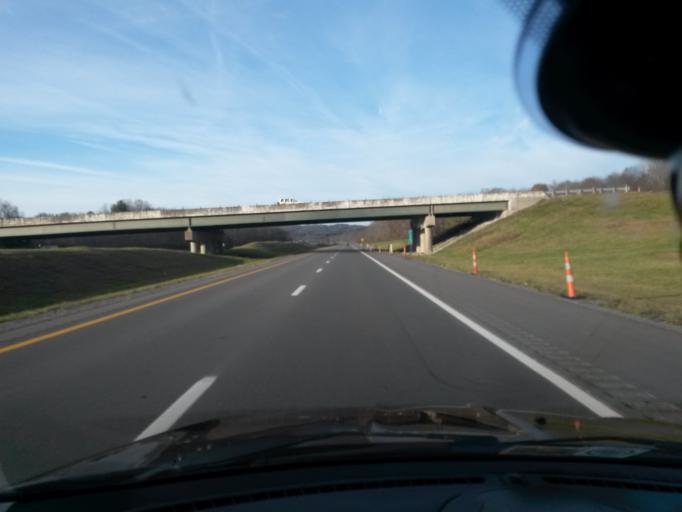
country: US
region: West Virginia
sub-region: Greenbrier County
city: Rainelle
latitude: 37.9042
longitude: -80.6324
